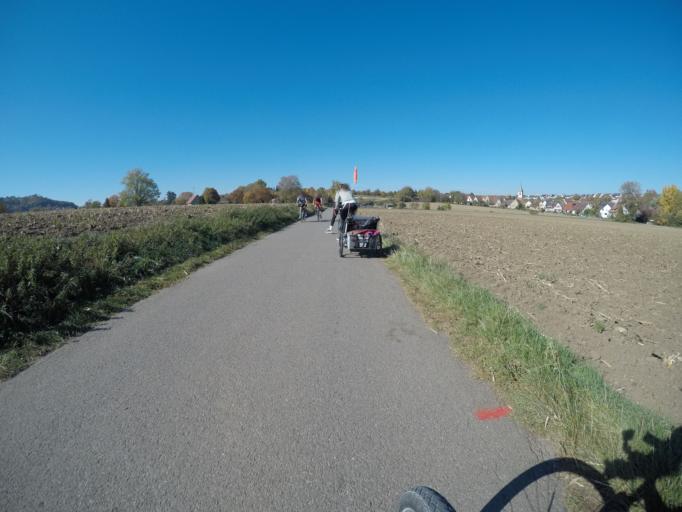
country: DE
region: Baden-Wuerttemberg
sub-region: Tuebingen Region
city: Rottenburg
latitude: 48.5308
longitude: 8.9504
